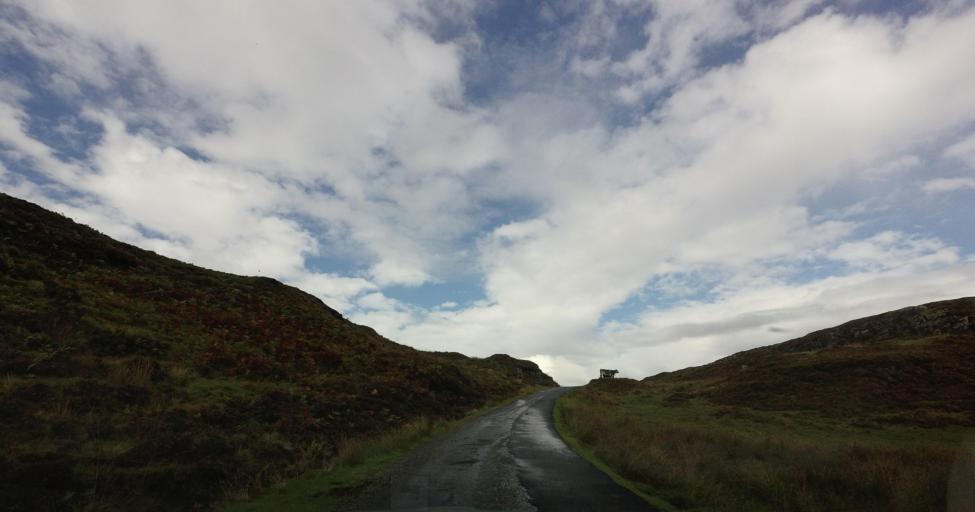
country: GB
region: Scotland
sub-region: Highland
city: Isle of Skye
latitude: 57.1440
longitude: -6.0906
